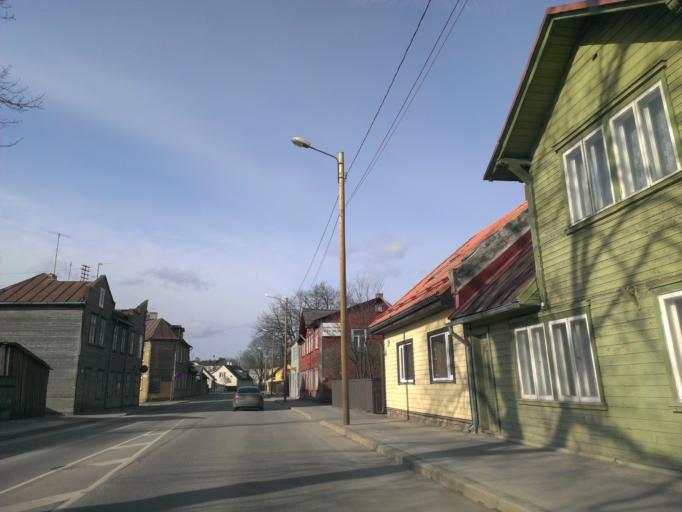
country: EE
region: Paernumaa
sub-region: Paernu linn
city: Parnu
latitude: 58.3939
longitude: 24.4946
